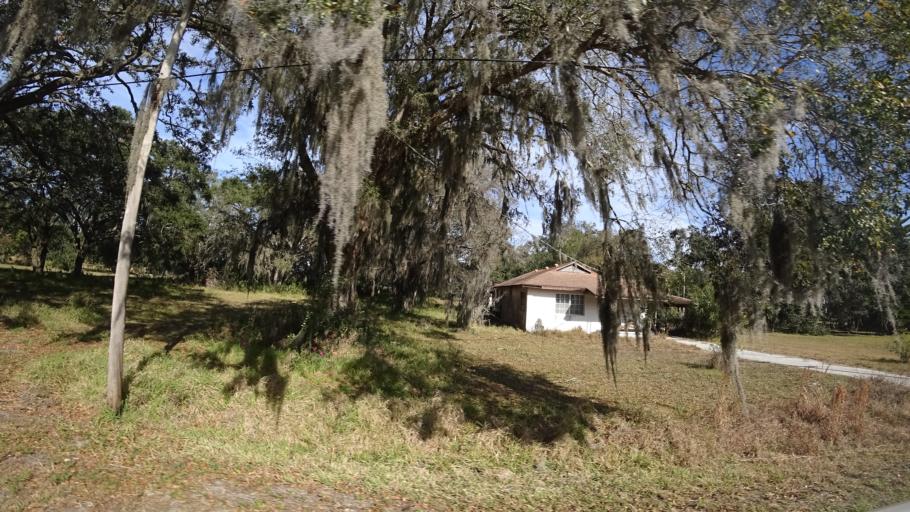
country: US
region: Florida
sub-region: Manatee County
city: Memphis
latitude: 27.6014
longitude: -82.5331
